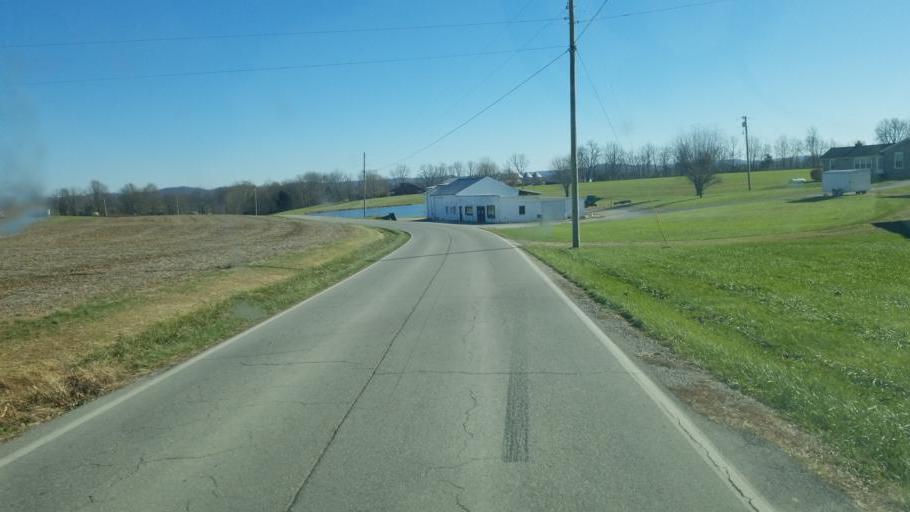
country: US
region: Kentucky
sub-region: Fleming County
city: Flemingsburg
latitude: 38.5344
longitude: -83.6273
